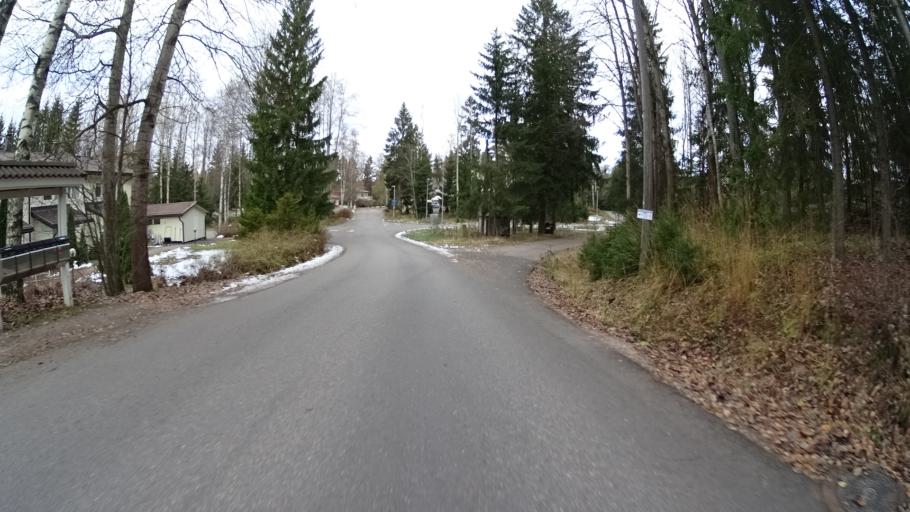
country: FI
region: Uusimaa
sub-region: Helsinki
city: Kilo
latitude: 60.2649
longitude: 24.8305
